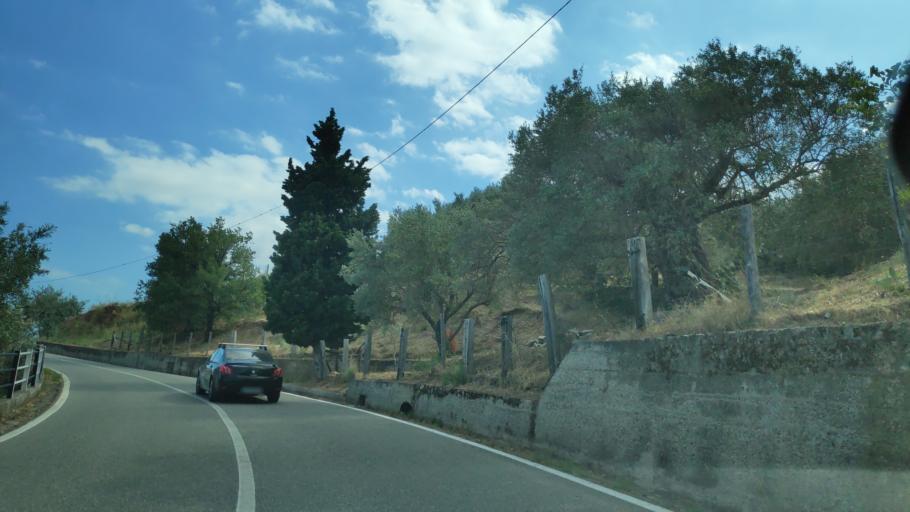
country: IT
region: Calabria
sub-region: Provincia di Catanzaro
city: Santa Caterina dello Ionio
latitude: 38.5253
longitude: 16.5370
